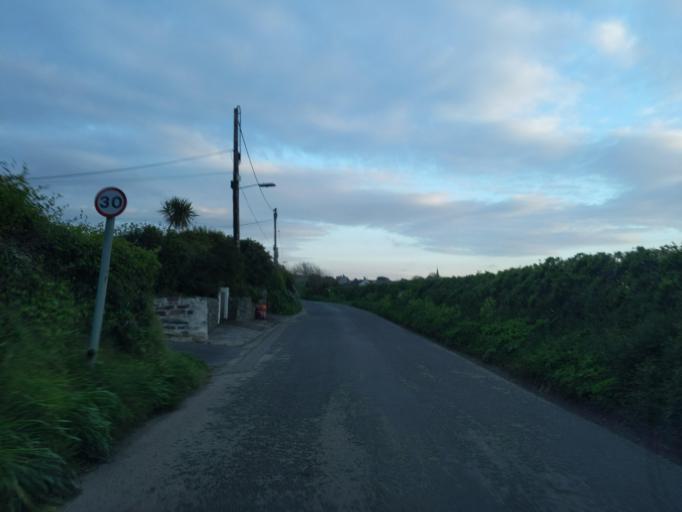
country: GB
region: England
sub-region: Cornwall
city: Polzeath
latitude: 50.5624
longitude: -4.8722
